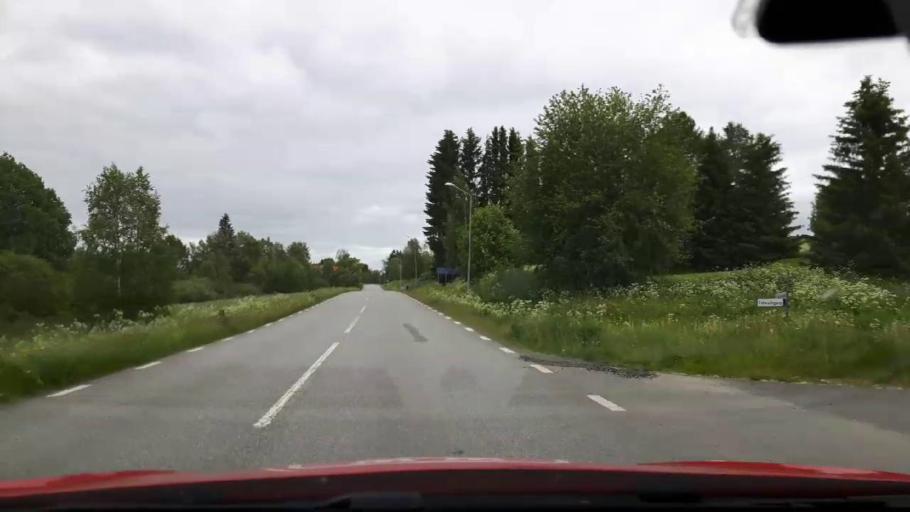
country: SE
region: Jaemtland
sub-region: Stroemsunds Kommun
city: Stroemsund
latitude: 63.5783
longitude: 15.3677
